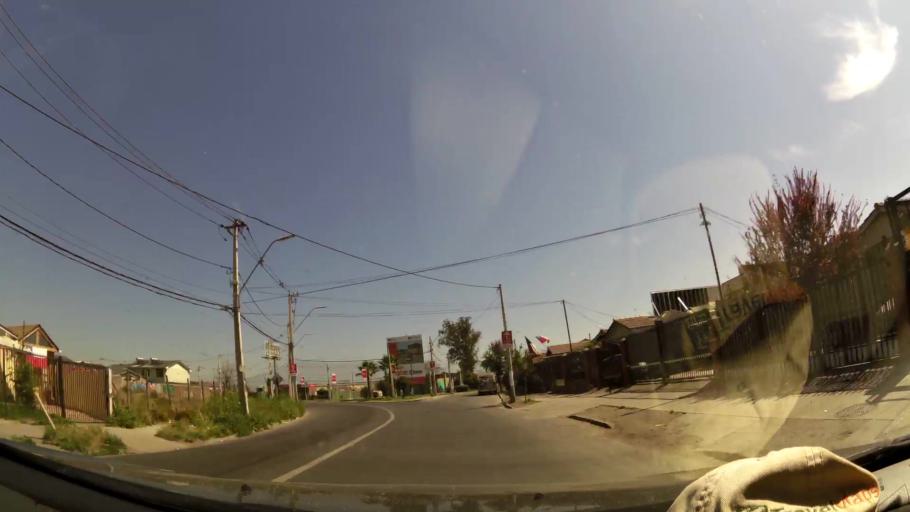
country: CL
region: Santiago Metropolitan
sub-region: Provincia de Santiago
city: Lo Prado
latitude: -33.3973
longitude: -70.7533
